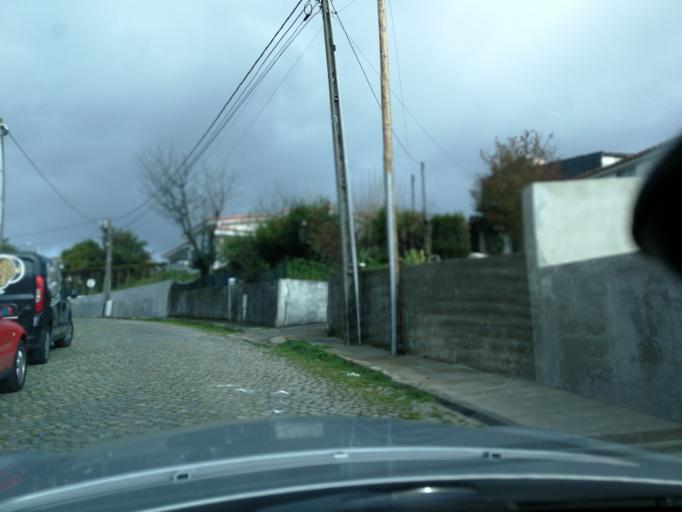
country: PT
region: Braga
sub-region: Braga
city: Braga
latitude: 41.5298
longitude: -8.4066
